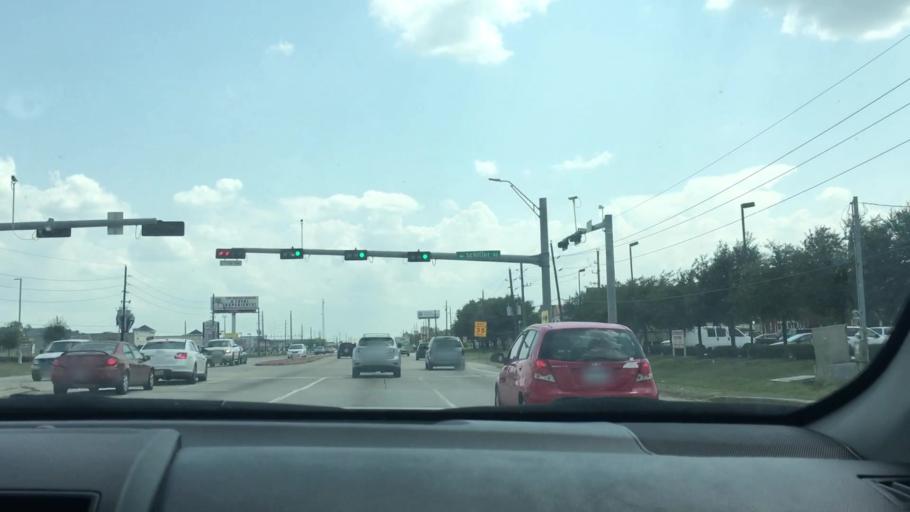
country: US
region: Texas
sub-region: Fort Bend County
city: Mission Bend
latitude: 29.7189
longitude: -95.6443
